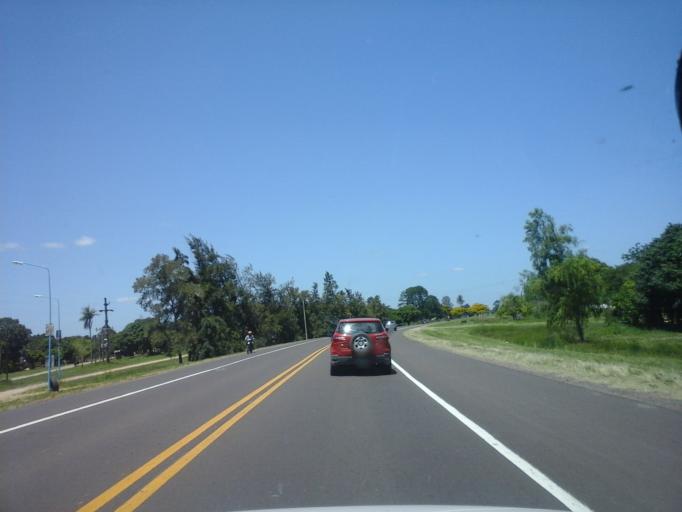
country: AR
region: Corrientes
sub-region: Departamento de San Cosme
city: San Cosme
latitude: -27.3773
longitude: -58.5103
